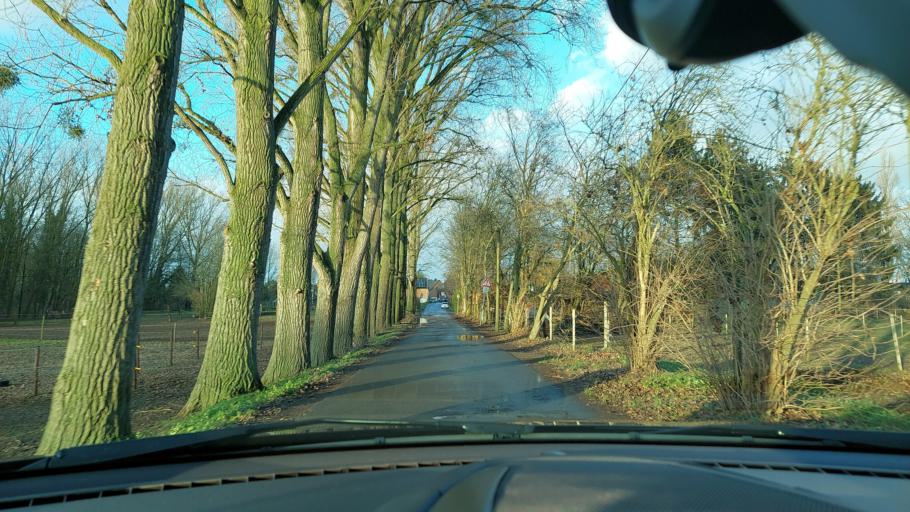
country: DE
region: North Rhine-Westphalia
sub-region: Regierungsbezirk Koln
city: Sinnersdorf
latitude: 51.0522
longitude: 6.8177
